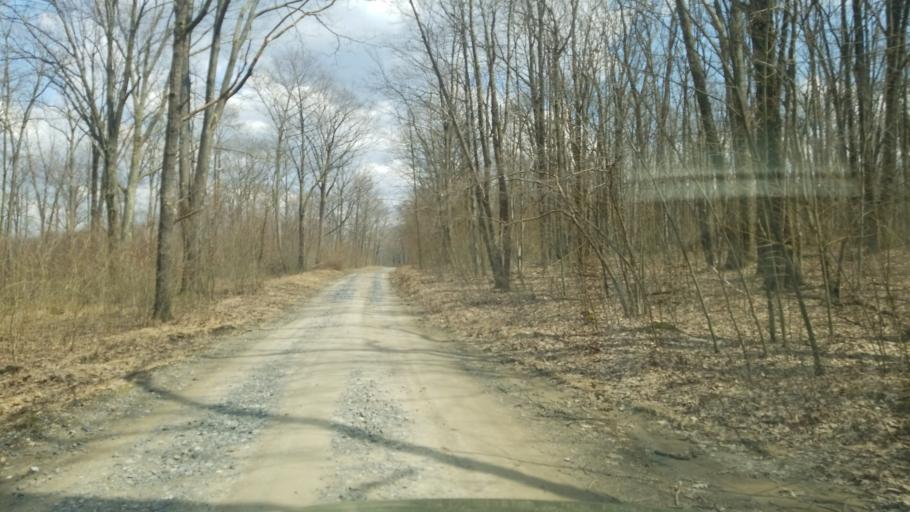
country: US
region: Pennsylvania
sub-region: Clearfield County
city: Clearfield
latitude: 41.1686
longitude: -78.5012
